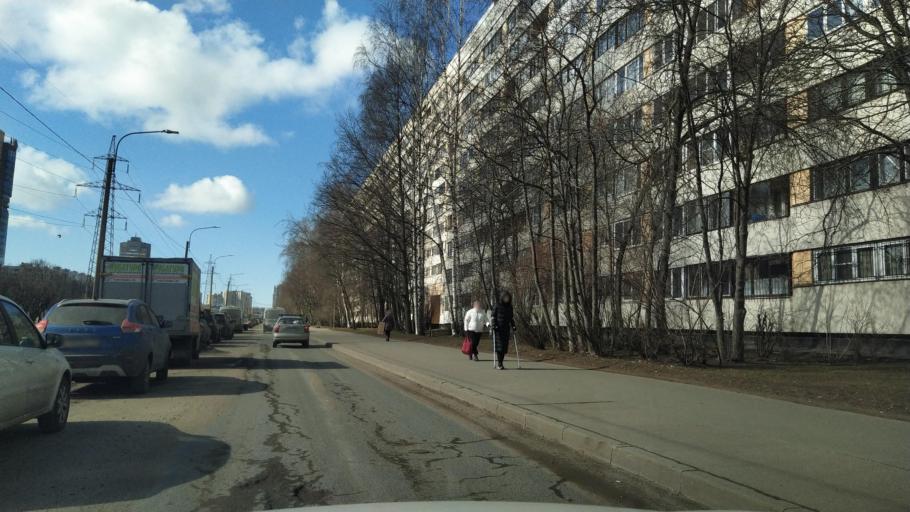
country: RU
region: St.-Petersburg
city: Komendantsky aerodrom
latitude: 60.0048
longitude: 30.2887
